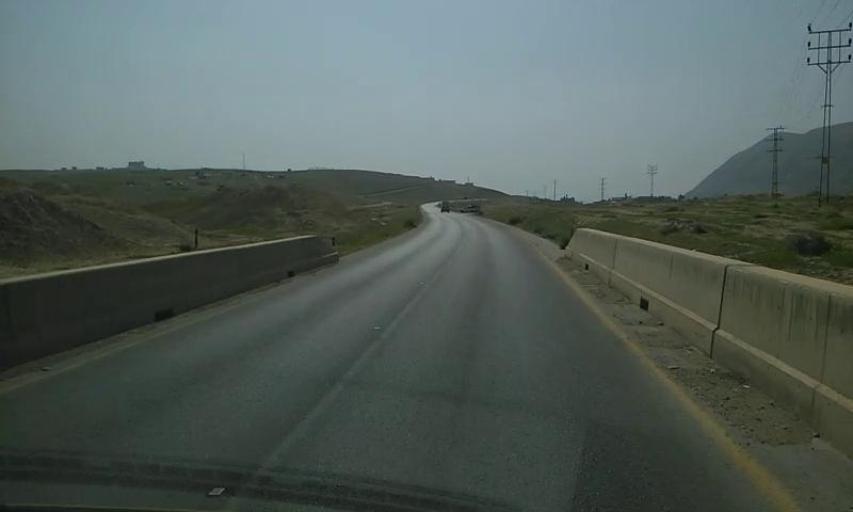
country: PS
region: West Bank
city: An Nuway`imah
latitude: 31.9018
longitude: 35.4261
